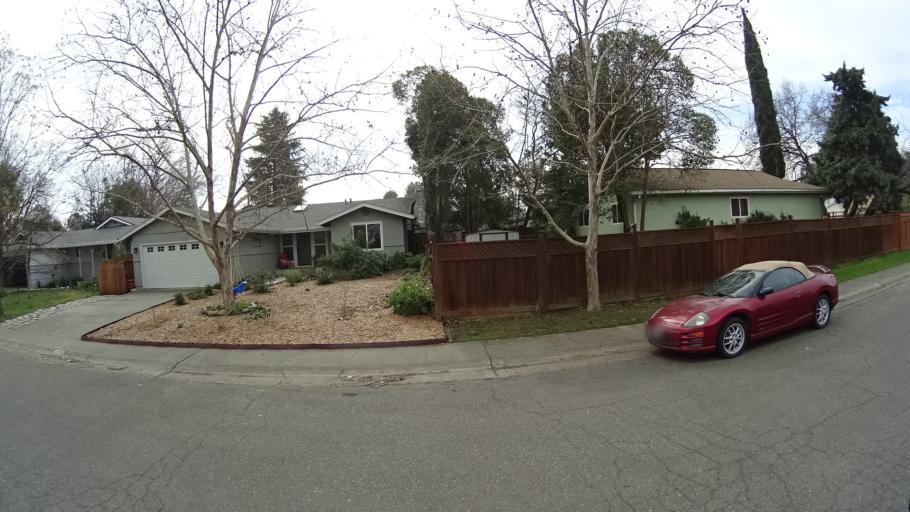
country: US
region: California
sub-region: Yolo County
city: Davis
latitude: 38.5598
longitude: -121.7338
